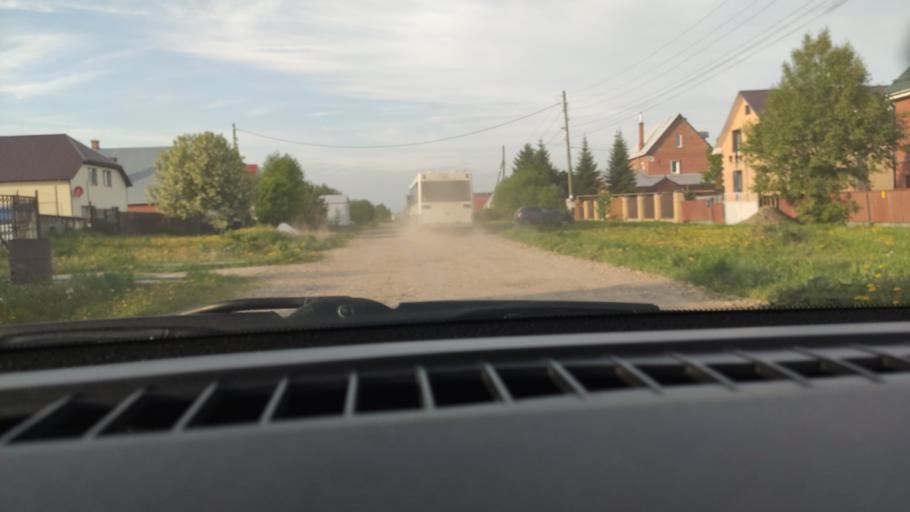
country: RU
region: Perm
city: Kultayevo
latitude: 57.9120
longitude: 55.9912
